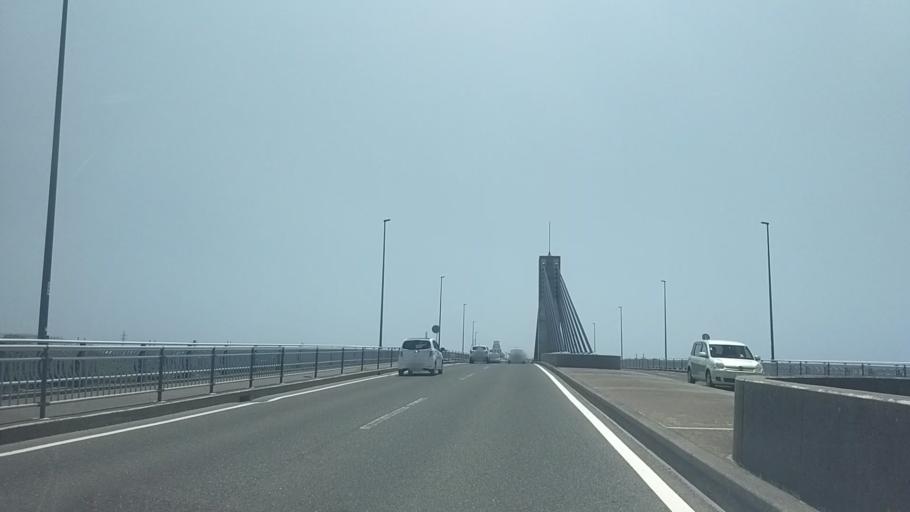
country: JP
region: Shizuoka
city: Hamamatsu
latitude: 34.6925
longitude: 137.6475
